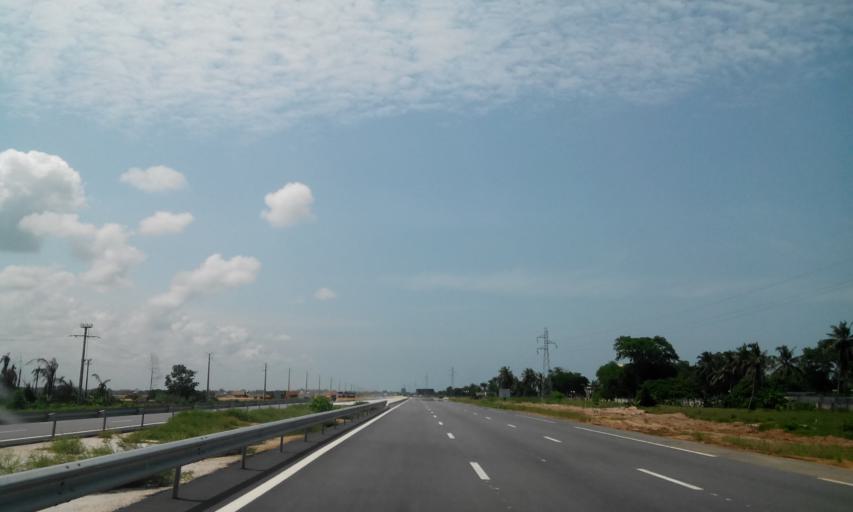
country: CI
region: Sud-Comoe
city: Grand-Bassam
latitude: 5.2323
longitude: -3.7612
